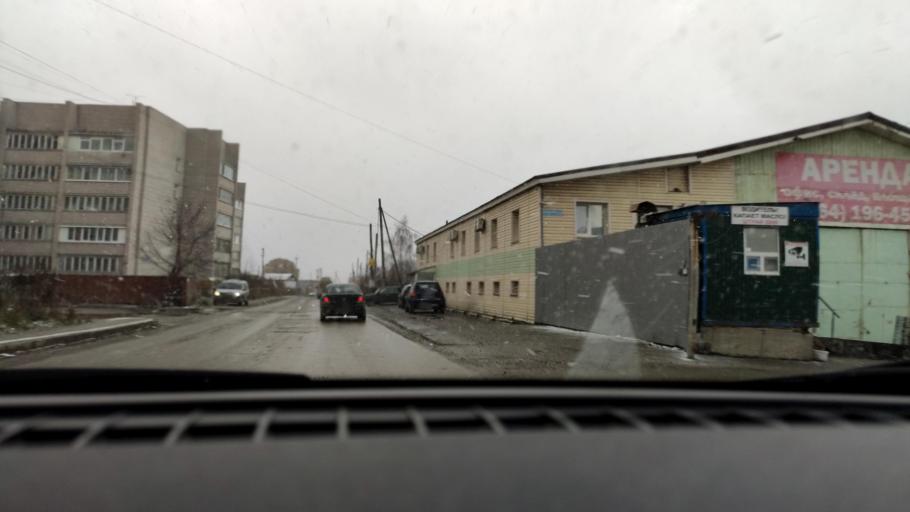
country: RU
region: Perm
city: Kondratovo
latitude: 57.9473
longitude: 56.0812
